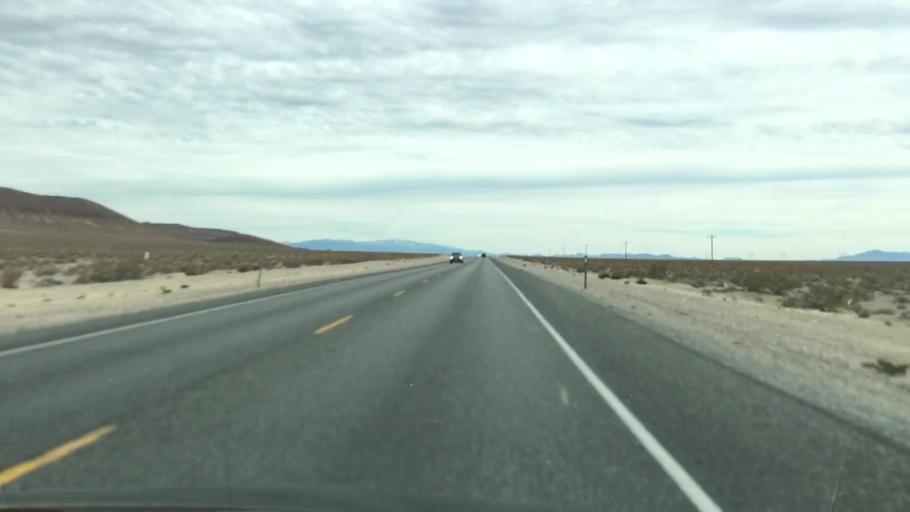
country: US
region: Nevada
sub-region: Nye County
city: Beatty
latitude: 36.7047
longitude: -116.5892
